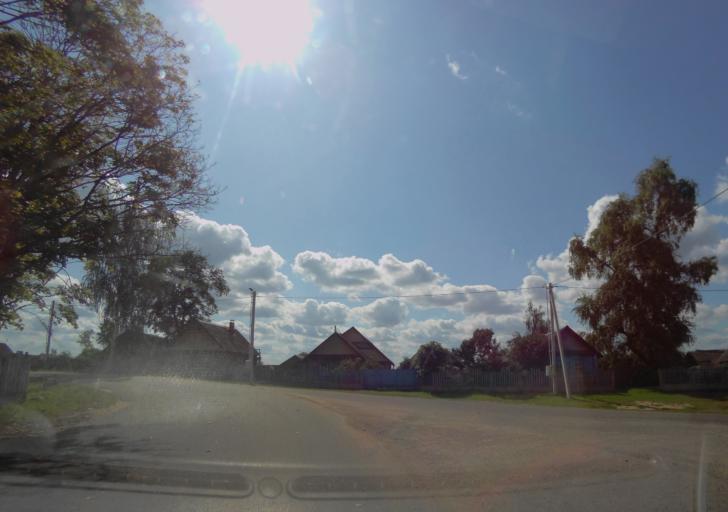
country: BY
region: Minsk
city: Horad Barysaw
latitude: 54.3868
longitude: 28.4721
